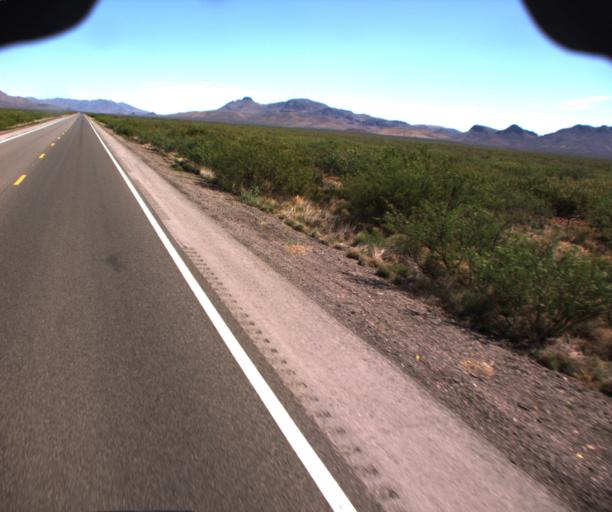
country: US
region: Arizona
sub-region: Cochise County
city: Douglas
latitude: 31.3939
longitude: -109.5093
